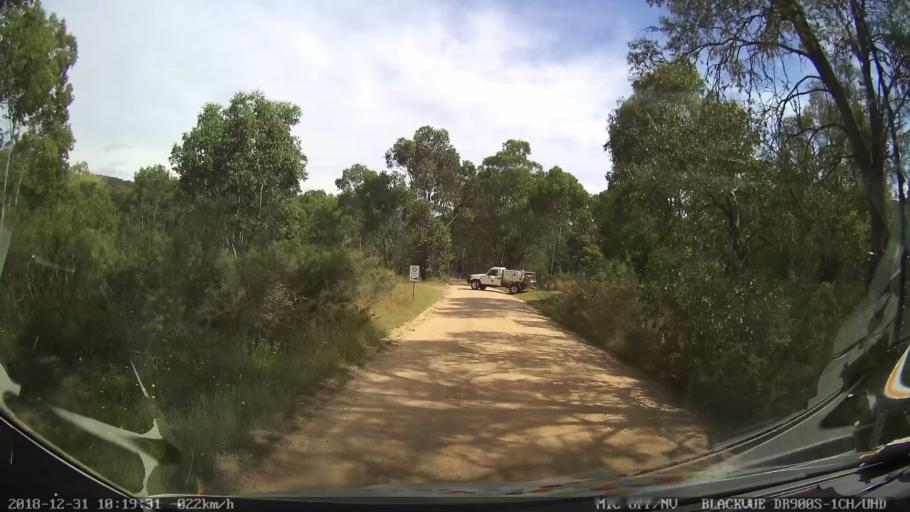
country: AU
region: New South Wales
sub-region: Snowy River
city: Jindabyne
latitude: -36.5402
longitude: 148.1346
